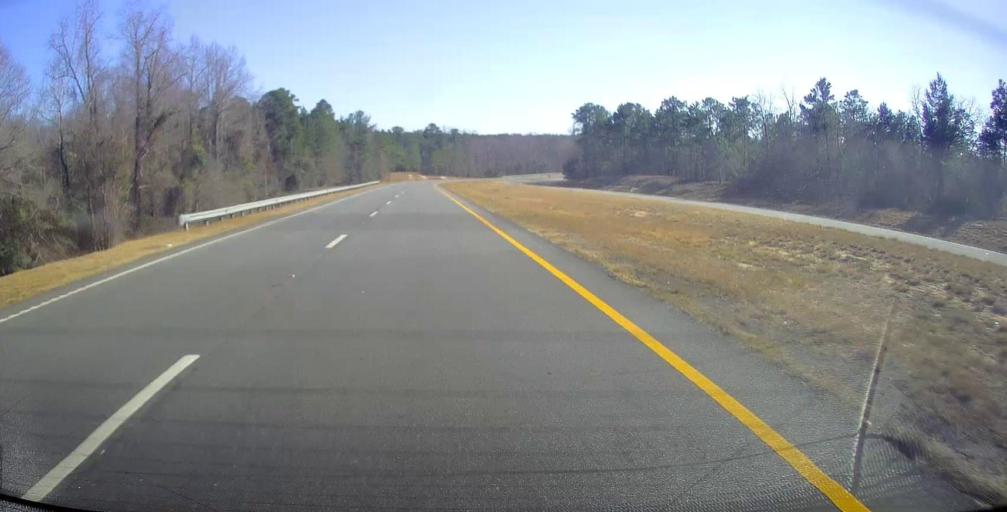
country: US
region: Georgia
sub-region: Taylor County
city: Butler
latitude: 32.5897
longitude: -84.2363
